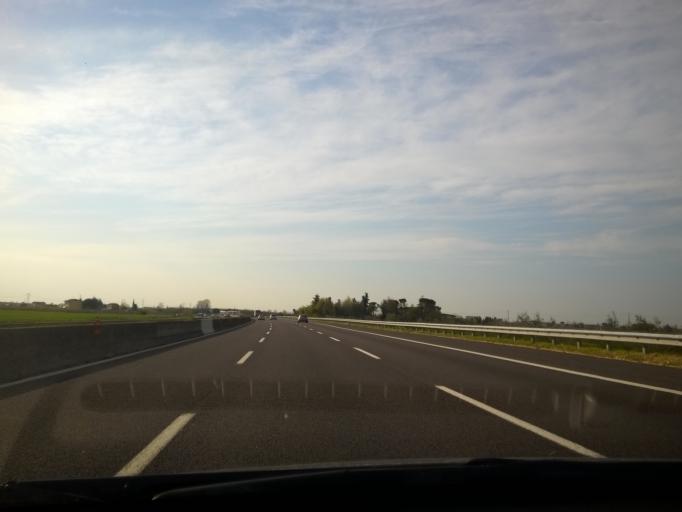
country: IT
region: Emilia-Romagna
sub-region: Forli-Cesena
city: Bagnarola
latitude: 44.1598
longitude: 12.3082
